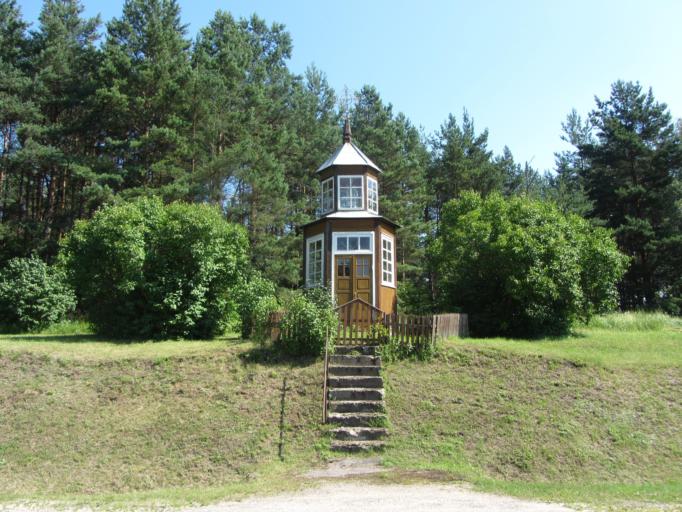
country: LT
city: Zarasai
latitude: 55.5843
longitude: 26.1264
